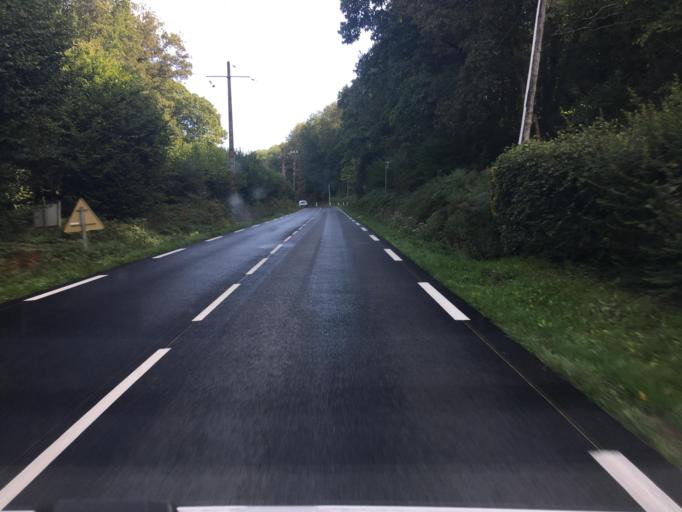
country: FR
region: Brittany
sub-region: Departement du Finistere
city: La Foret-Fouesnant
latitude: 47.9154
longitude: -3.9442
